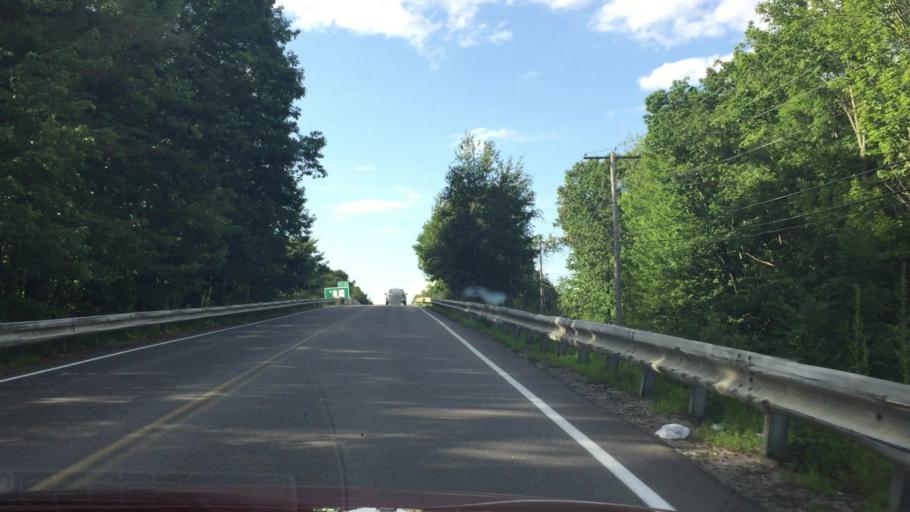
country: US
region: Maine
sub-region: Cumberland County
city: South Portland Gardens
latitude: 43.6273
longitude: -70.3475
